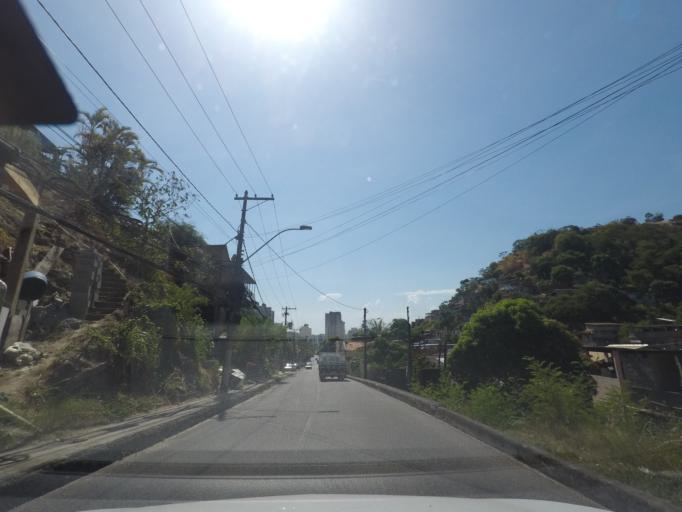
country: BR
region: Rio de Janeiro
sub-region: Niteroi
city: Niteroi
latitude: -22.9061
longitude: -43.0824
